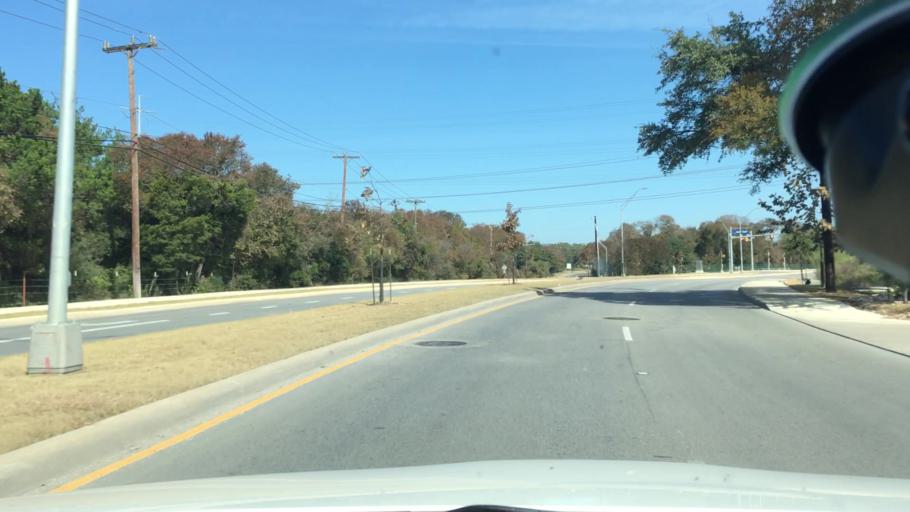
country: US
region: Texas
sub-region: Bexar County
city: Hollywood Park
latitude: 29.5943
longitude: -98.4242
